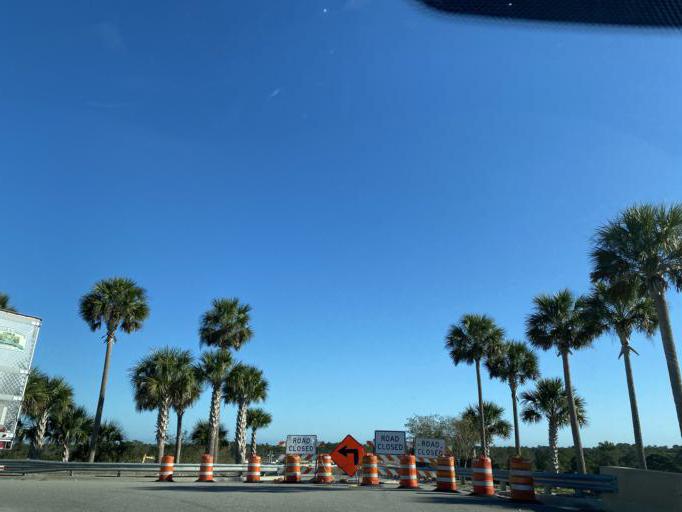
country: US
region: Florida
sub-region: Lake County
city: Mount Plymouth
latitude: 28.8097
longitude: -81.5079
